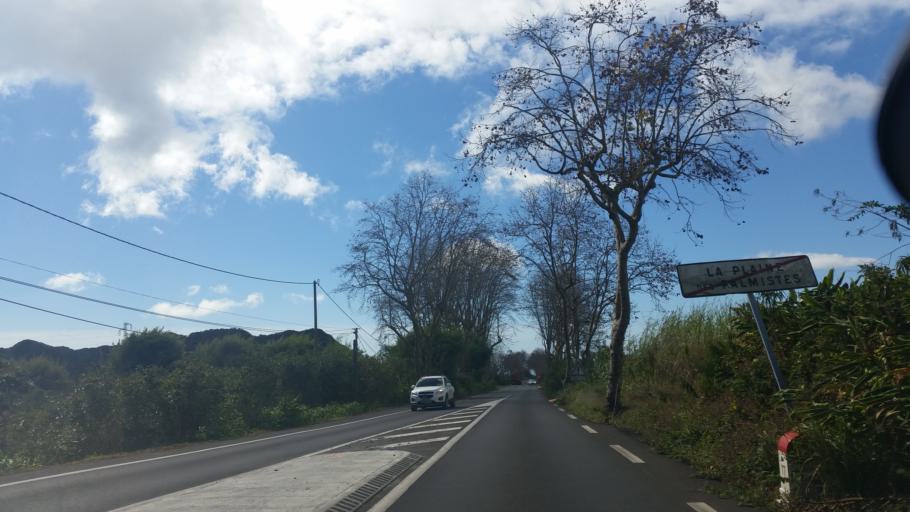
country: RE
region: Reunion
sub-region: Reunion
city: Saint-Benoit
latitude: -21.1212
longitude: 55.6427
